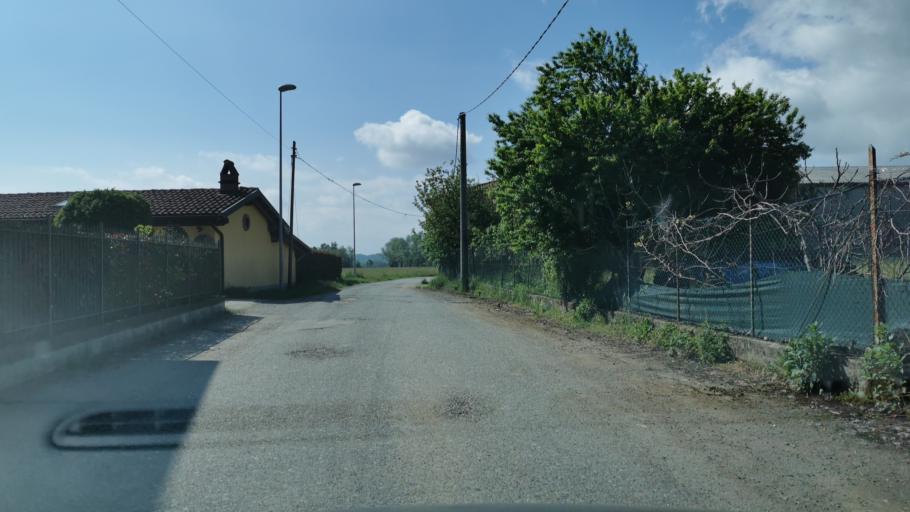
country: IT
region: Piedmont
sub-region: Provincia di Torino
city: Front
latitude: 45.2874
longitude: 7.7000
